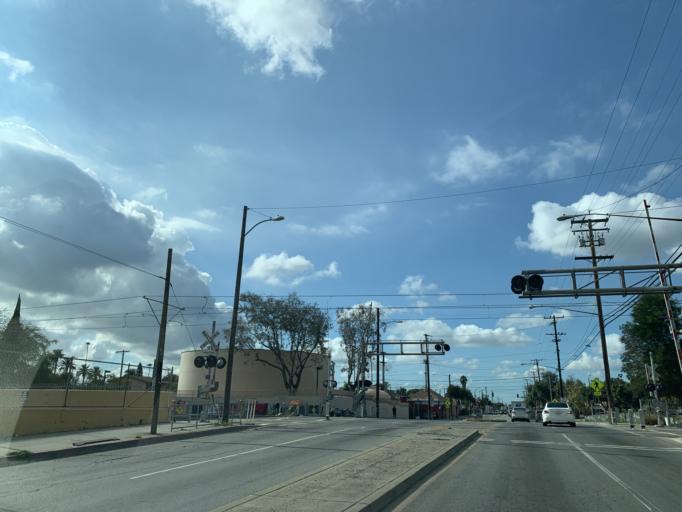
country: US
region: California
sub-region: Los Angeles County
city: Florence-Graham
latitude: 33.9821
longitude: -118.2429
